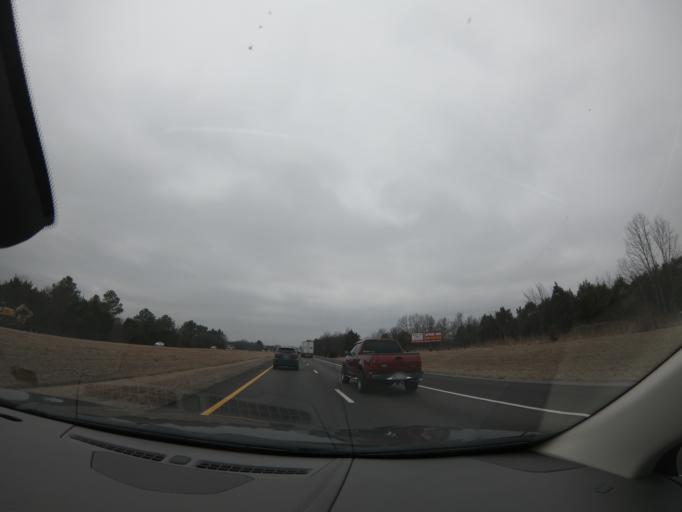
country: US
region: Tennessee
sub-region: Rutherford County
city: Plainview
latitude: 35.7660
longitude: -86.3573
